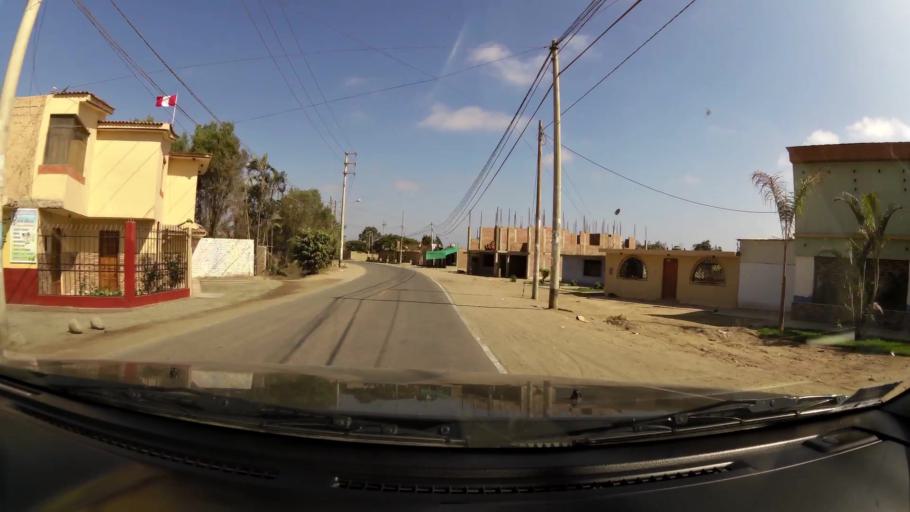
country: PE
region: Ica
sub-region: Provincia de Chincha
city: Sunampe
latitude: -13.4200
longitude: -76.1584
